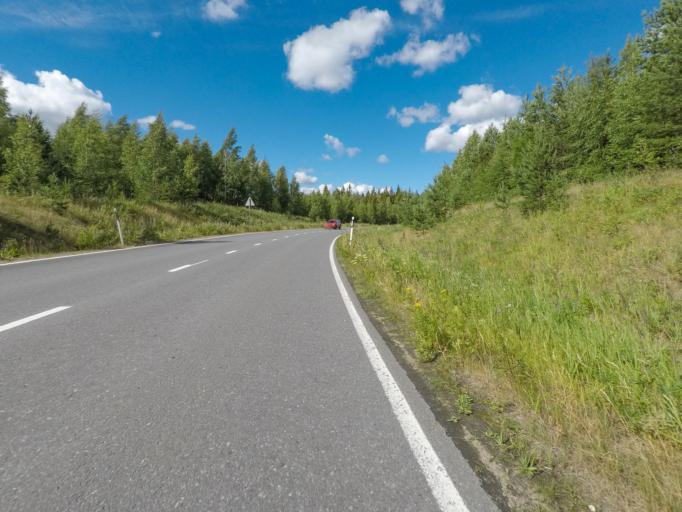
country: FI
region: South Karelia
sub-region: Lappeenranta
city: Joutseno
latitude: 61.0926
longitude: 28.3524
